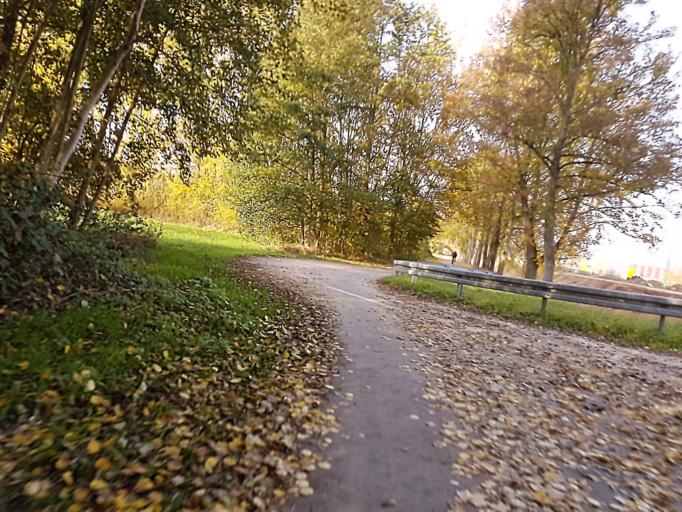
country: DE
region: Bavaria
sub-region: Regierungsbezirk Unterfranken
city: Kleinwallstadt
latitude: 49.8629
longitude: 9.1570
